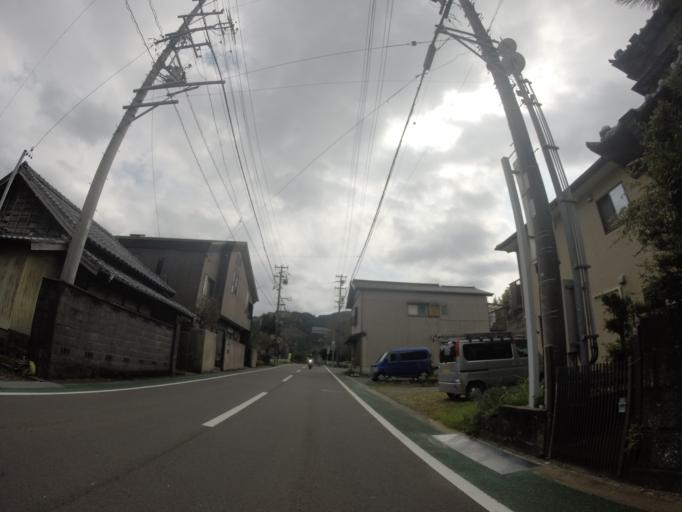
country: JP
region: Shizuoka
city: Fujieda
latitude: 34.9024
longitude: 138.1991
